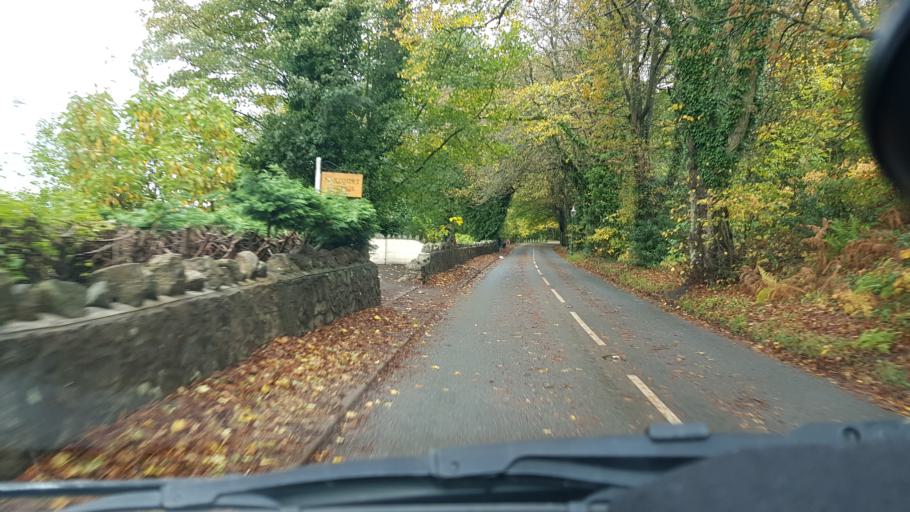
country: GB
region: England
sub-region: Worcestershire
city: Great Malvern
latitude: 52.1057
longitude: -2.3453
